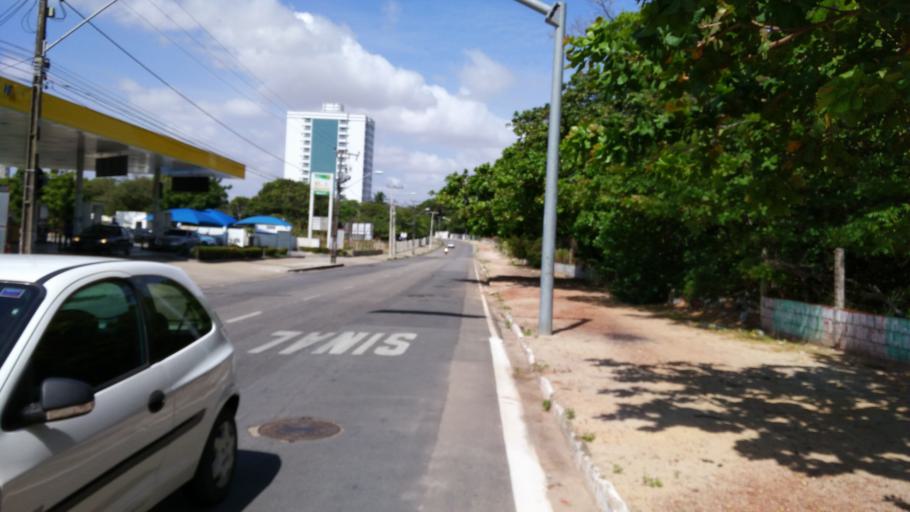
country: BR
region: Ceara
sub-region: Fortaleza
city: Fortaleza
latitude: -3.7707
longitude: -38.4885
